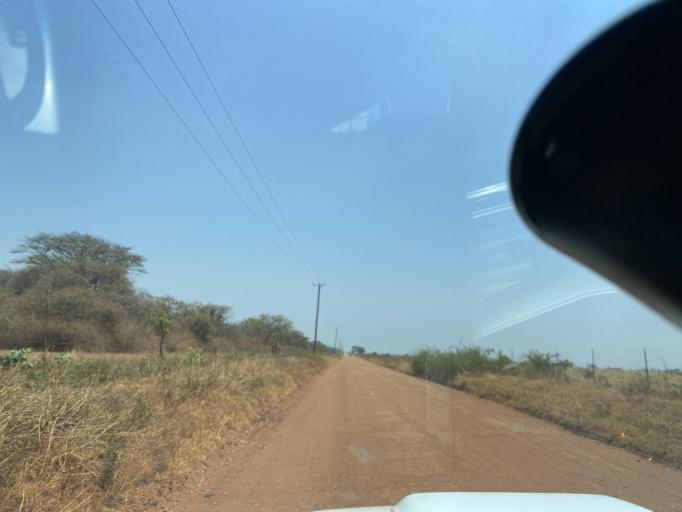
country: ZM
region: Lusaka
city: Lusaka
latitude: -15.4361
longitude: 28.0722
